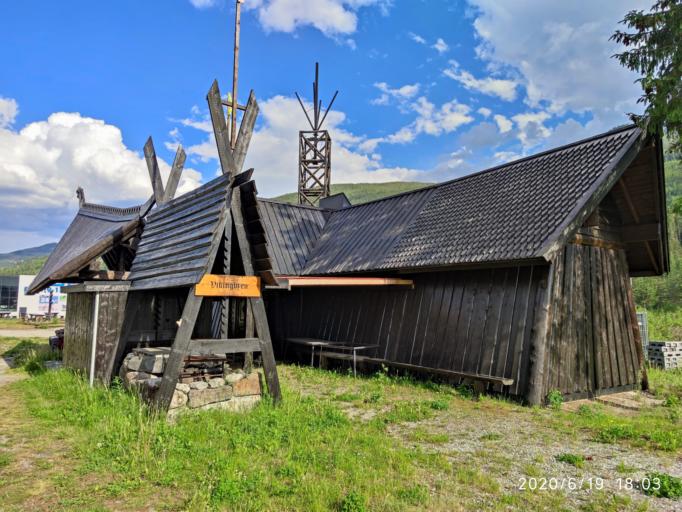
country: NO
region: Buskerud
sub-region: Gol
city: Gol
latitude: 60.6979
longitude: 8.9486
